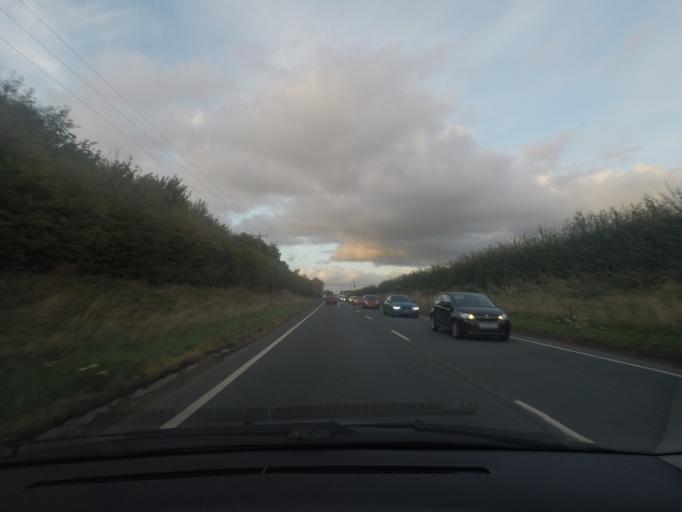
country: GB
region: England
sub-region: City of York
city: Nether Poppleton
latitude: 53.9686
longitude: -1.1462
